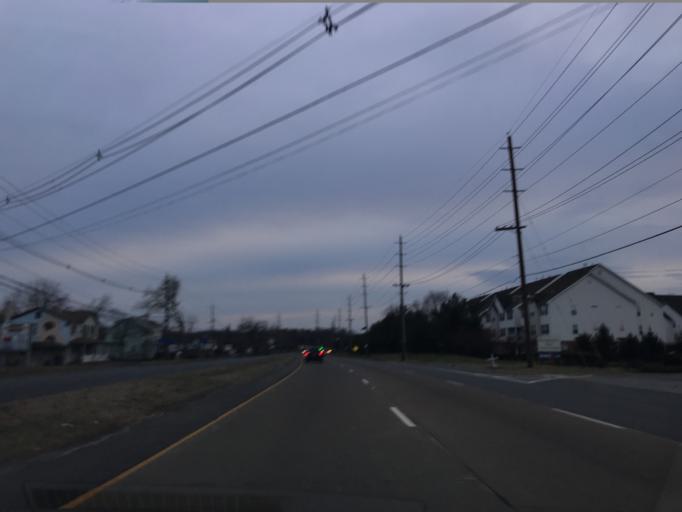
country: US
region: New Jersey
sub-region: Middlesex County
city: Dayton
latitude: 40.4250
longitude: -74.4960
